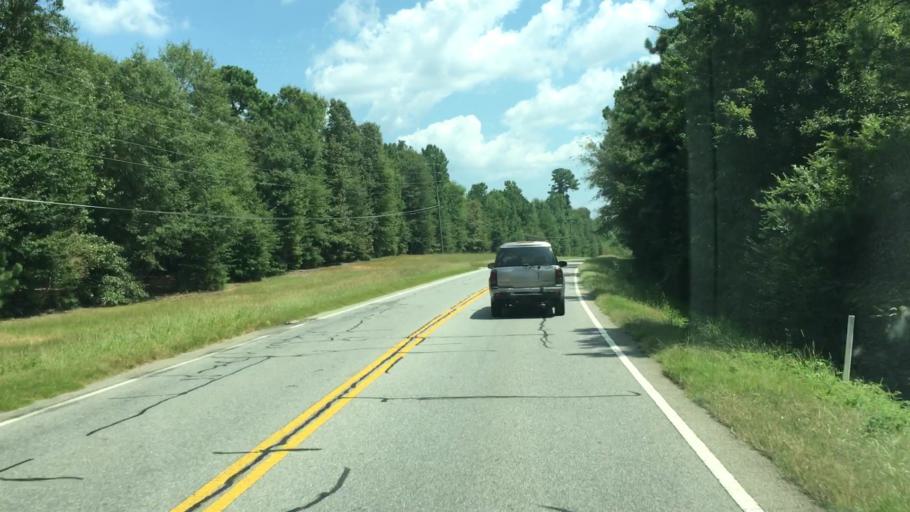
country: US
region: Georgia
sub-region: Barrow County
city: Statham
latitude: 33.9079
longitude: -83.5850
